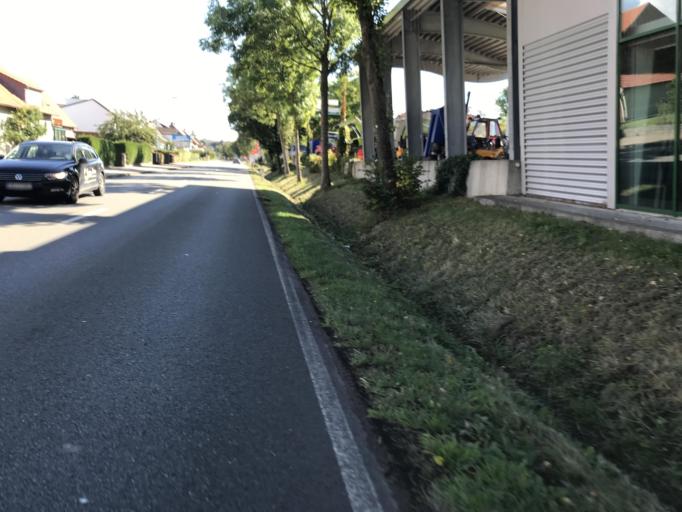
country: DE
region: Hesse
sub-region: Regierungsbezirk Kassel
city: Vohl
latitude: 51.2559
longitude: 8.9358
